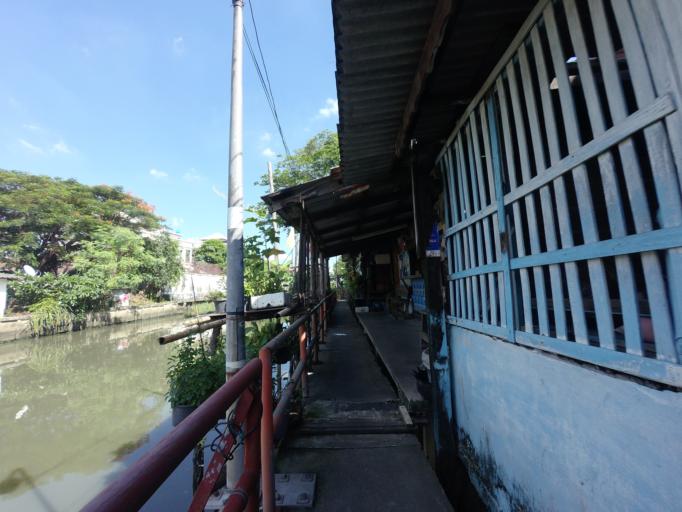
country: TH
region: Bangkok
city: Huai Khwang
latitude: 13.7913
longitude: 100.5894
